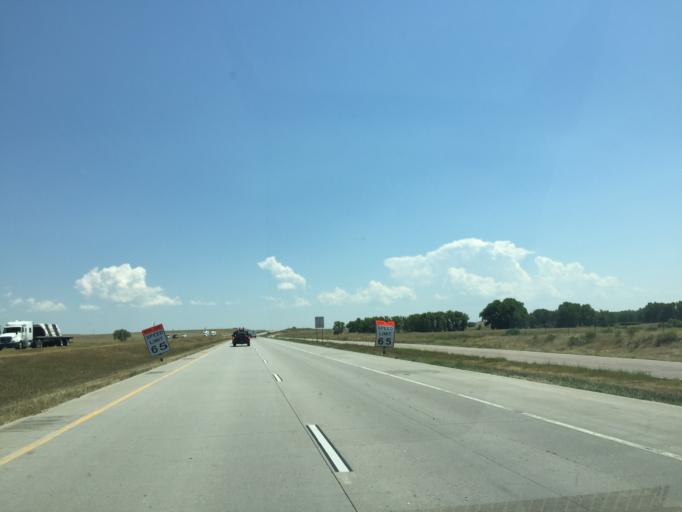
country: US
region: Colorado
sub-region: Arapahoe County
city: Byers
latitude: 39.4958
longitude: -103.9640
